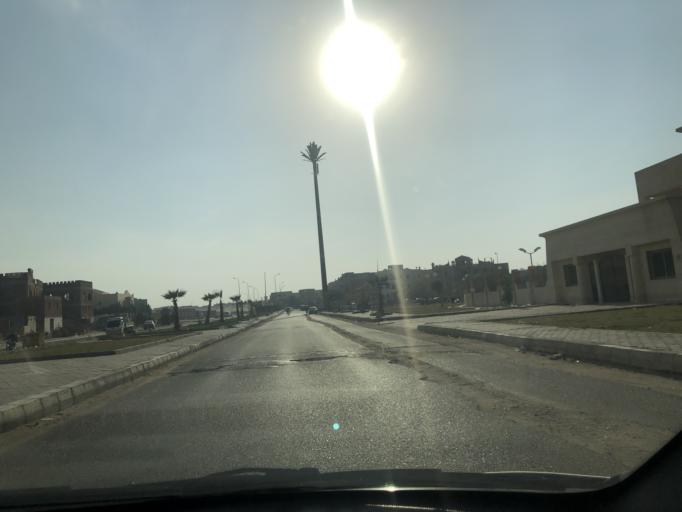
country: EG
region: Al Jizah
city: Madinat Sittah Uktubar
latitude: 29.9054
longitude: 30.9362
